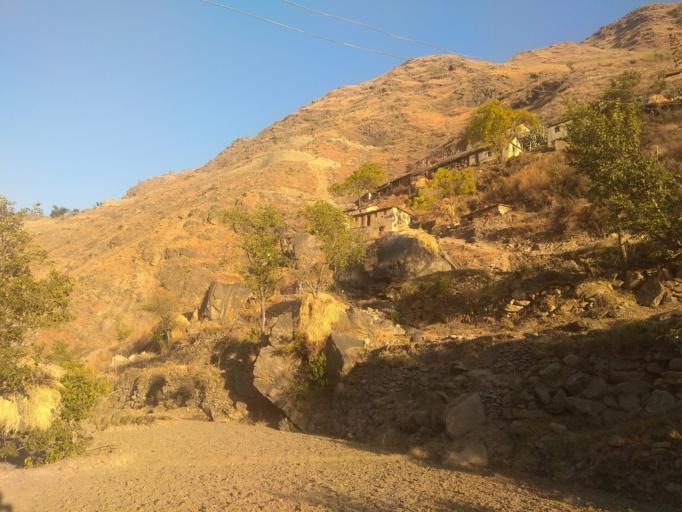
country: NP
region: Mid Western
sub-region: Bheri Zone
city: Dailekh
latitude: 29.2789
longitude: 81.7323
